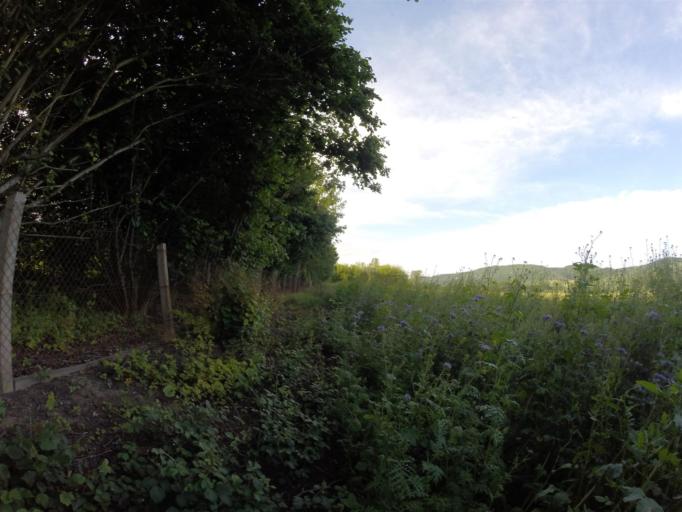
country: DE
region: Thuringia
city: Neuengonna
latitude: 50.9716
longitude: 11.6544
